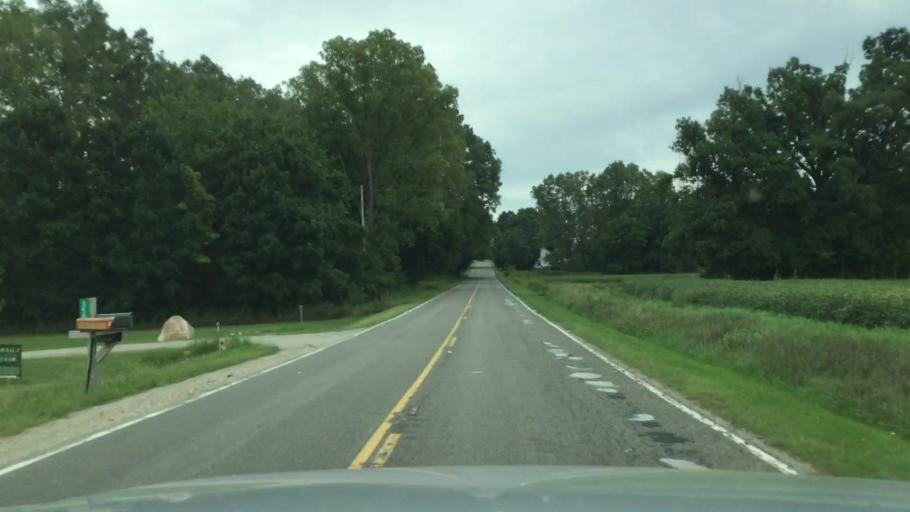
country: US
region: Michigan
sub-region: Shiawassee County
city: Corunna
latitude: 42.9355
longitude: -84.0956
